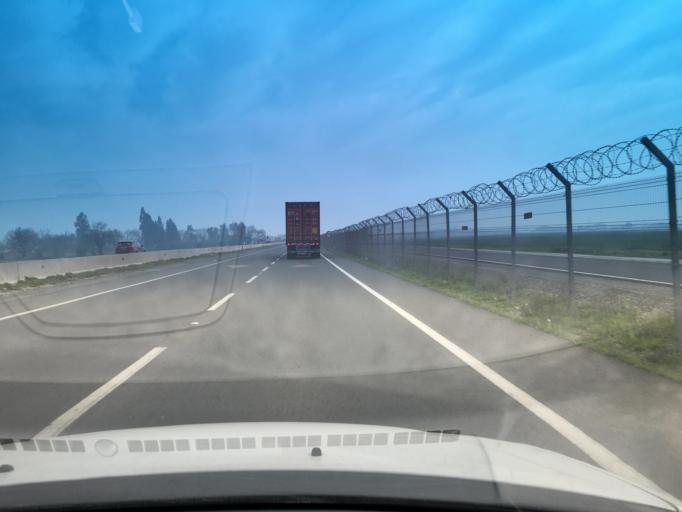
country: CL
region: Santiago Metropolitan
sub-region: Provincia de Santiago
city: Lo Prado
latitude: -33.3726
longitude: -70.8054
